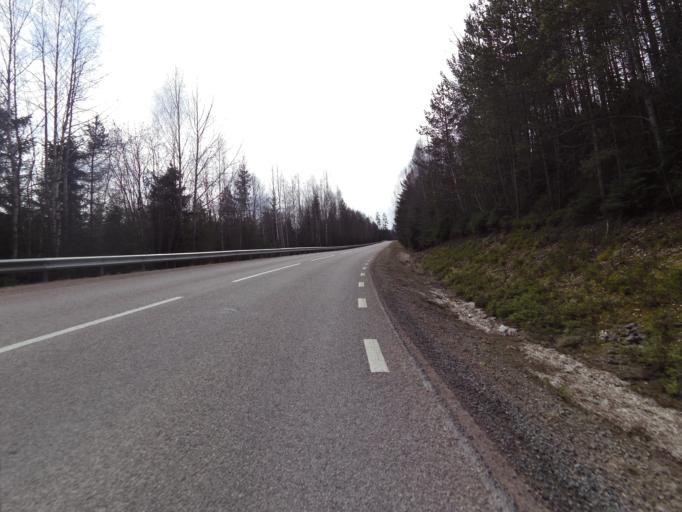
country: SE
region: Dalarna
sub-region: Hedemora Kommun
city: Langshyttan
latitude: 60.5396
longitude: 16.1306
